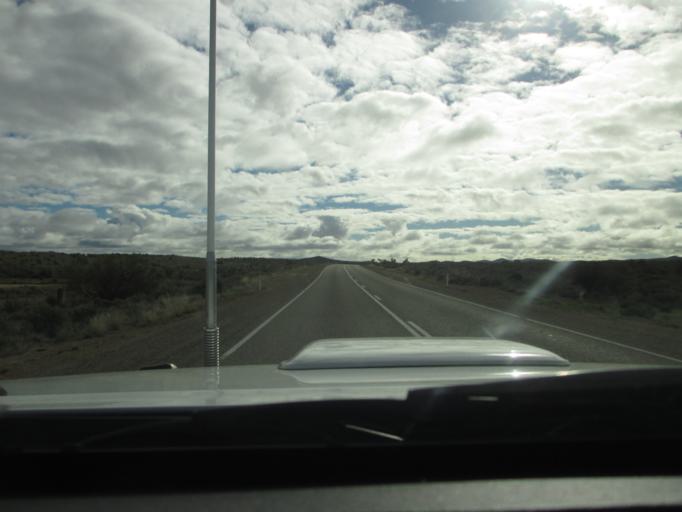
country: AU
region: South Australia
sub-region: Flinders Ranges
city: Quorn
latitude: -32.2896
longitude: 138.4918
